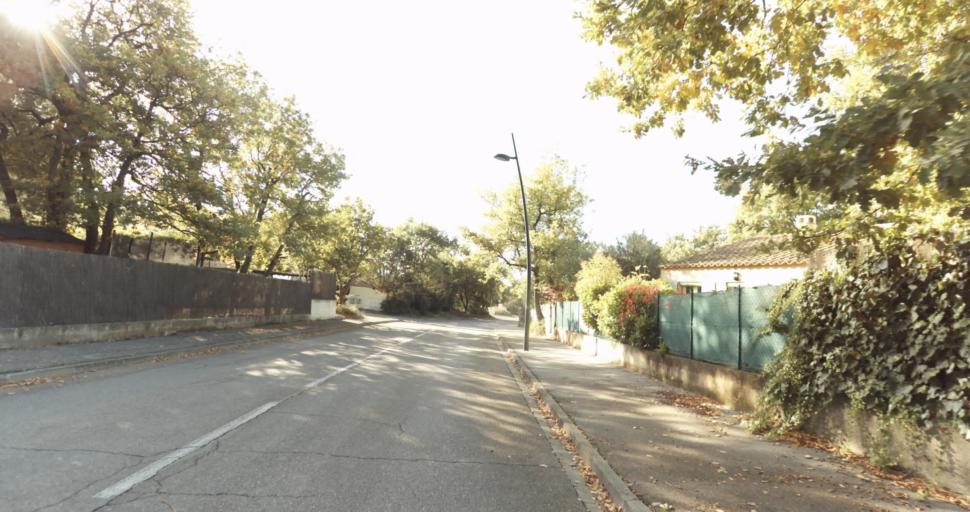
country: FR
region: Provence-Alpes-Cote d'Azur
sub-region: Departement des Bouches-du-Rhone
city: Venelles
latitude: 43.5940
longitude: 5.4726
